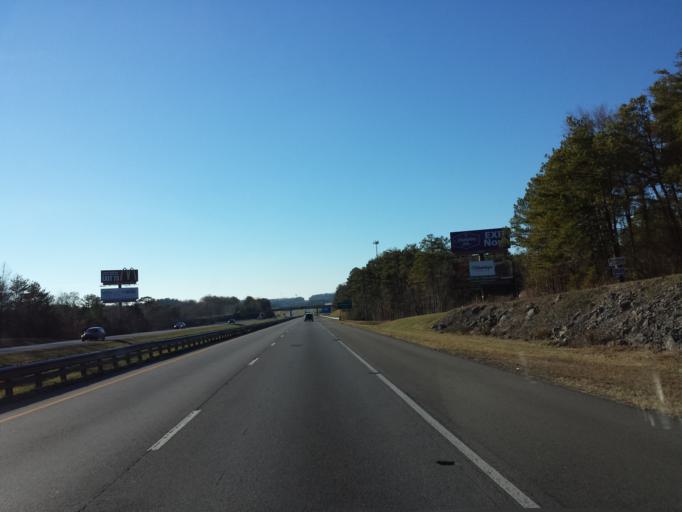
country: US
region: Alabama
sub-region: Tuscaloosa County
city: Holt
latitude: 33.1720
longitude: -87.4316
